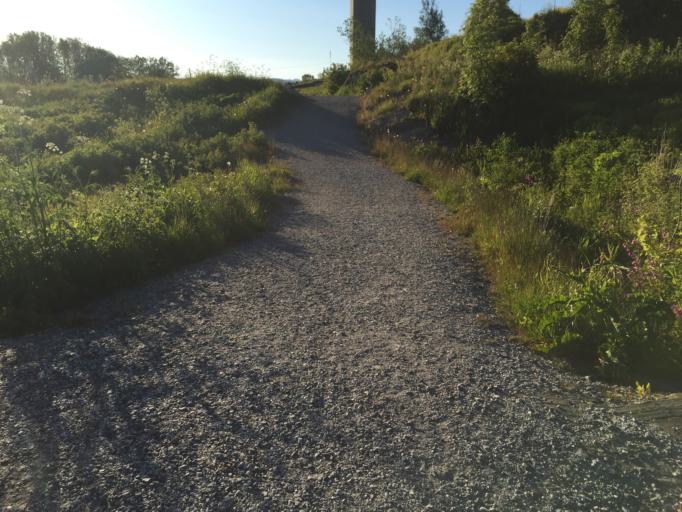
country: NO
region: Nordland
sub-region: Bodo
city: Loding
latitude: 67.2317
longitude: 14.6184
